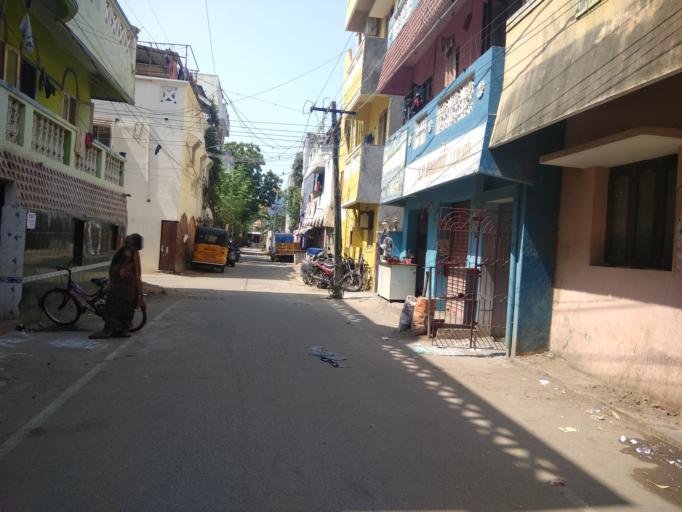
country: IN
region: Tamil Nadu
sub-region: Kancheepuram
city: Alandur
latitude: 12.9927
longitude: 80.2151
